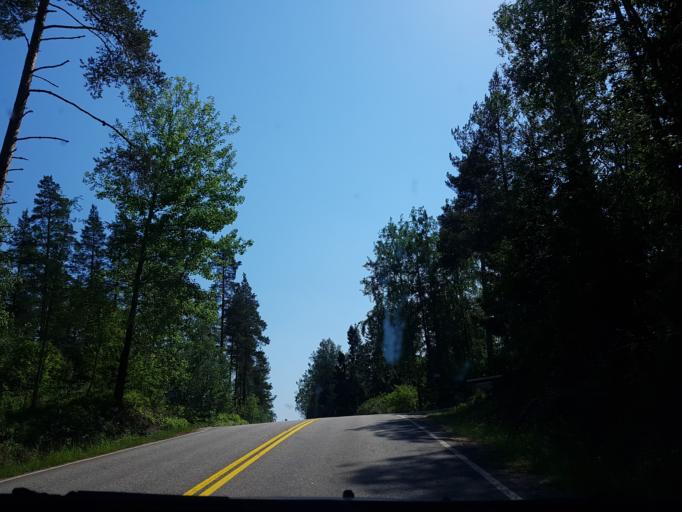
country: FI
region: Uusimaa
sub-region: Helsinki
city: Vihti
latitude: 60.3027
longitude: 24.4003
